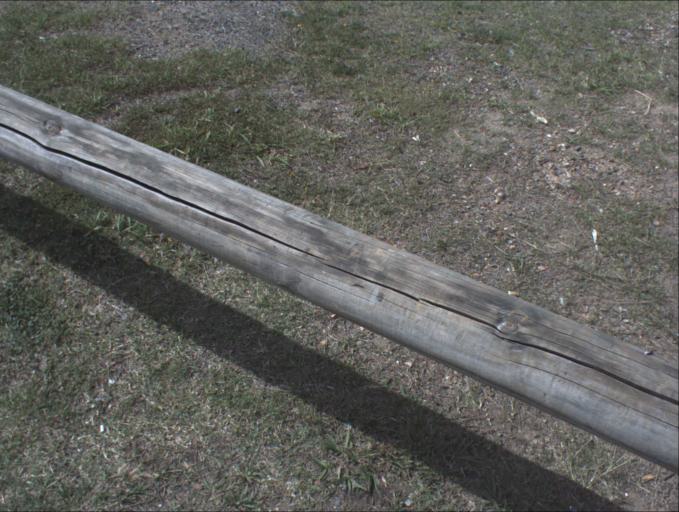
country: AU
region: Queensland
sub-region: Brisbane
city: Sunnybank Hills
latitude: -27.6636
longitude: 153.0511
